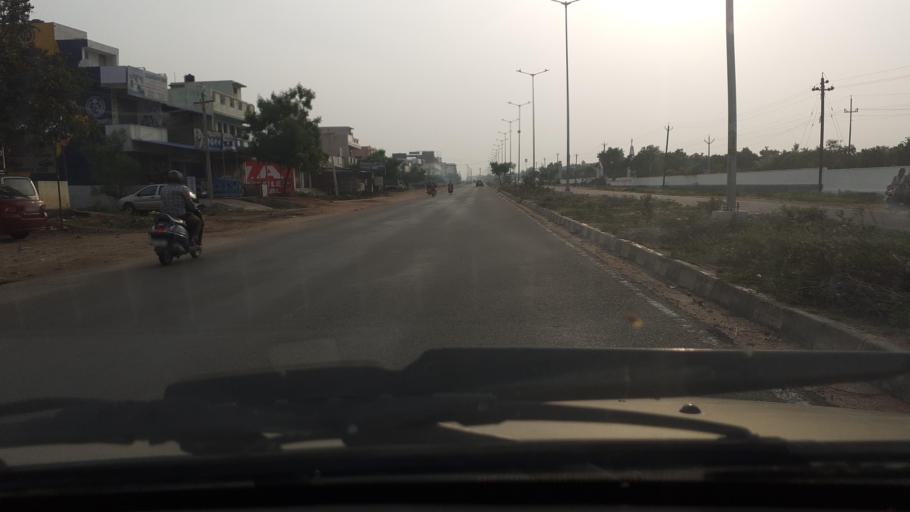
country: IN
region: Tamil Nadu
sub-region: Tirunelveli Kattabo
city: Tirunelveli
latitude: 8.7138
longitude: 77.7865
